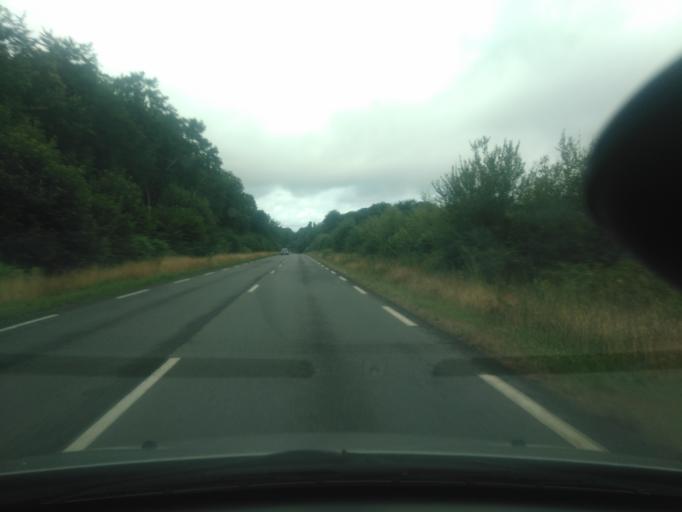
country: FR
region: Brittany
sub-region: Departement des Cotes-d'Armor
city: Les Champs-Geraux
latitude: 48.4413
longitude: -1.9602
